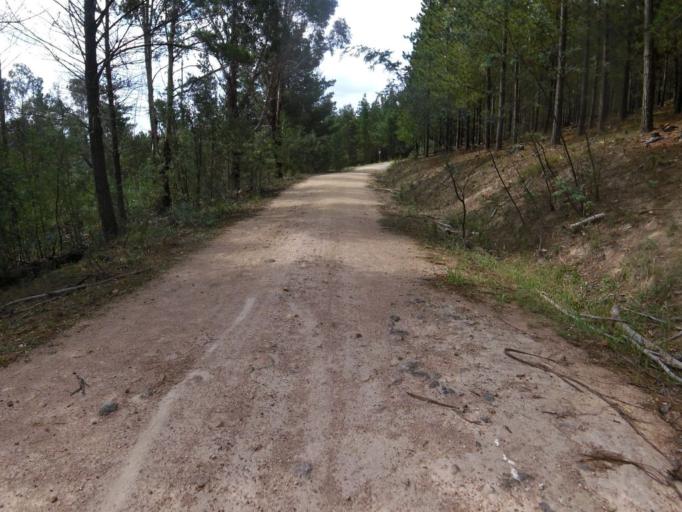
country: AU
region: Australian Capital Territory
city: Macarthur
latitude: -35.3833
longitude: 149.1207
